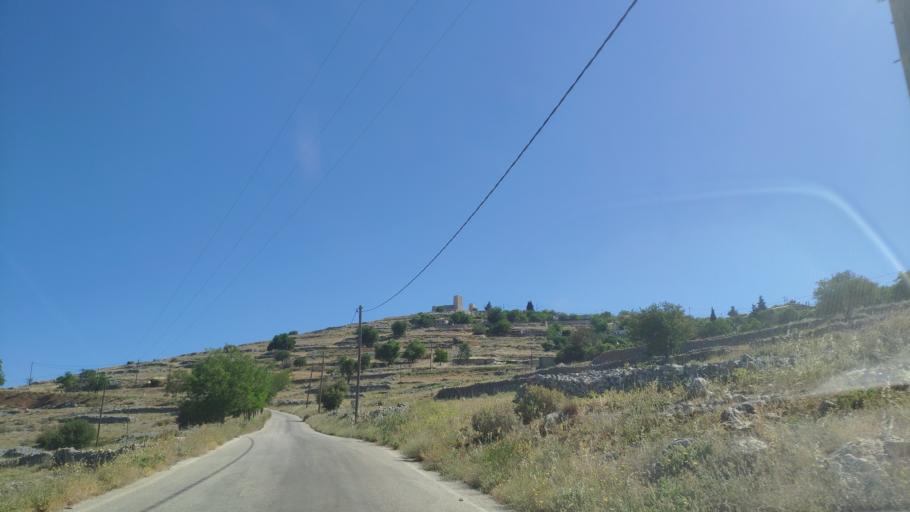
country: GR
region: Peloponnese
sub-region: Nomos Korinthias
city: Khiliomodhi
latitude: 37.7523
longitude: 22.8760
